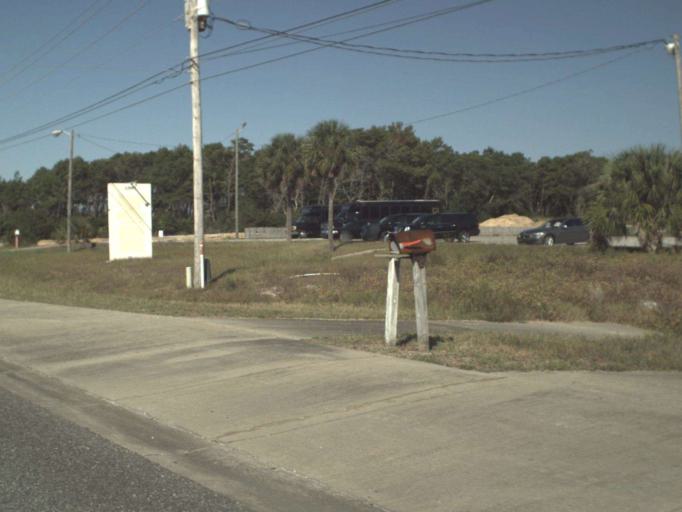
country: US
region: Florida
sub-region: Bay County
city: Laguna Beach
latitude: 30.2742
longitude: -85.9980
